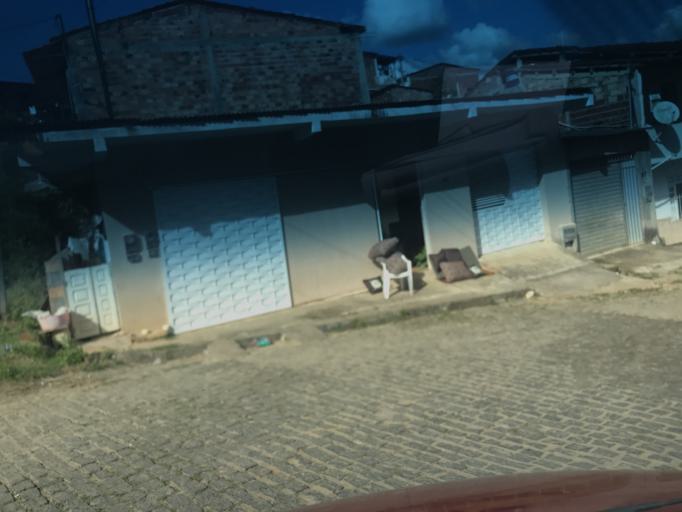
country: BR
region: Bahia
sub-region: Gandu
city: Gandu
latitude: -13.7466
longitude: -39.4920
